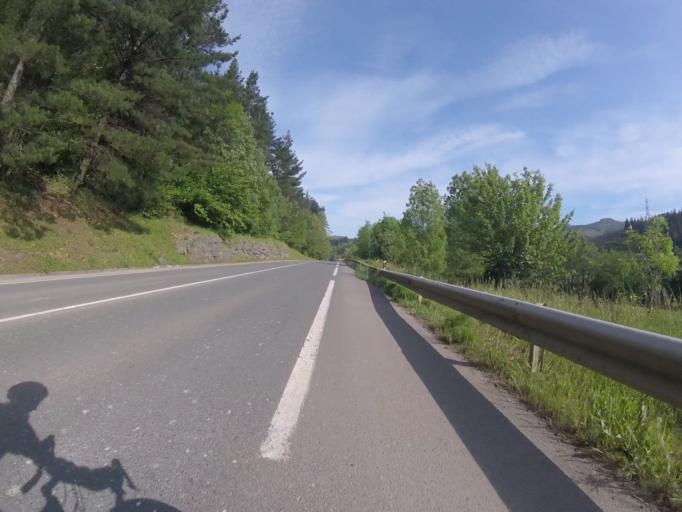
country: ES
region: Basque Country
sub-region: Provincia de Guipuzcoa
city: Gabiria
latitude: 43.0569
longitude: -2.2673
